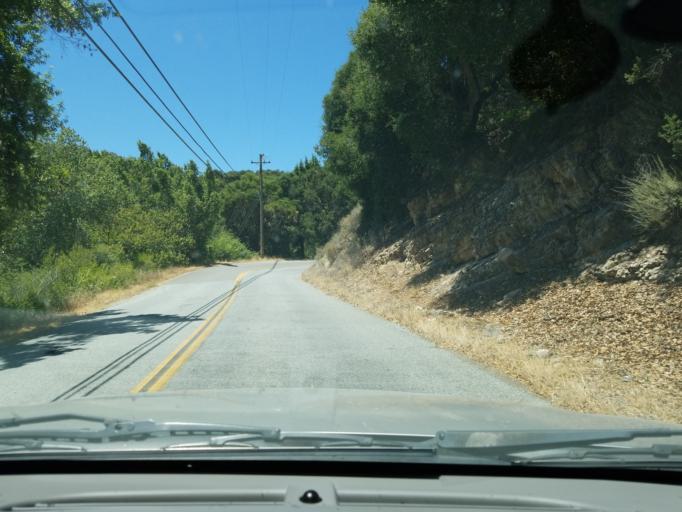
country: US
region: California
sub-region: Monterey County
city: Carmel Valley Village
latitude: 36.4553
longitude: -121.7045
